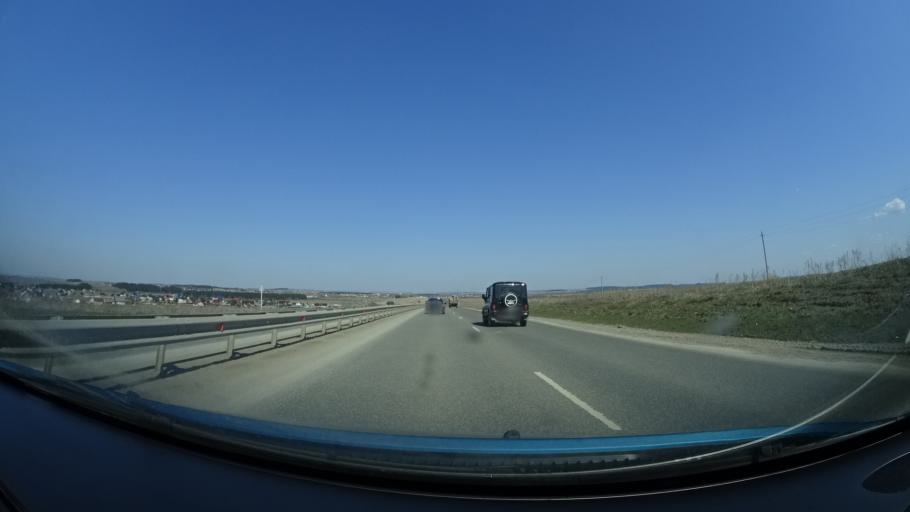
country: RU
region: Perm
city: Kultayevo
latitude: 57.8696
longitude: 55.8911
